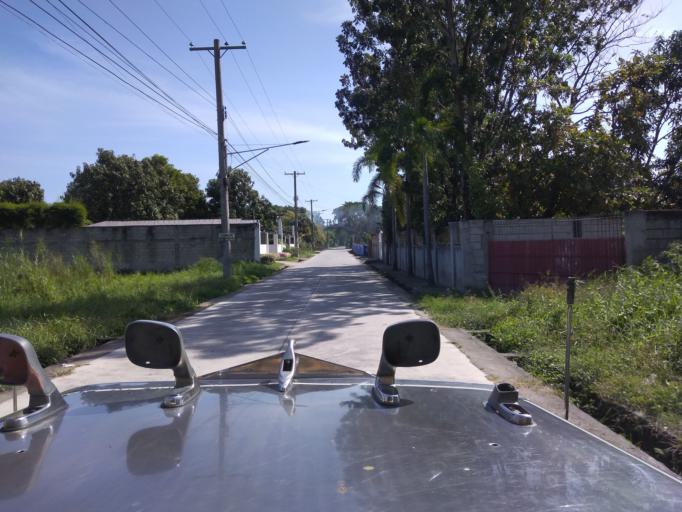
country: PH
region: Central Luzon
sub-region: Province of Pampanga
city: Bacolor
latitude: 15.0059
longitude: 120.6625
